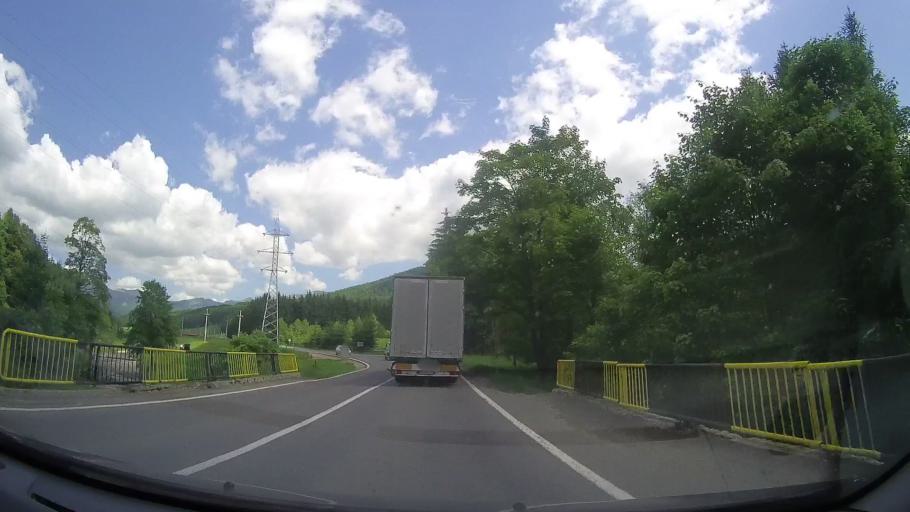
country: RO
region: Prahova
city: Maneciu
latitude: 45.4140
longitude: 25.9423
